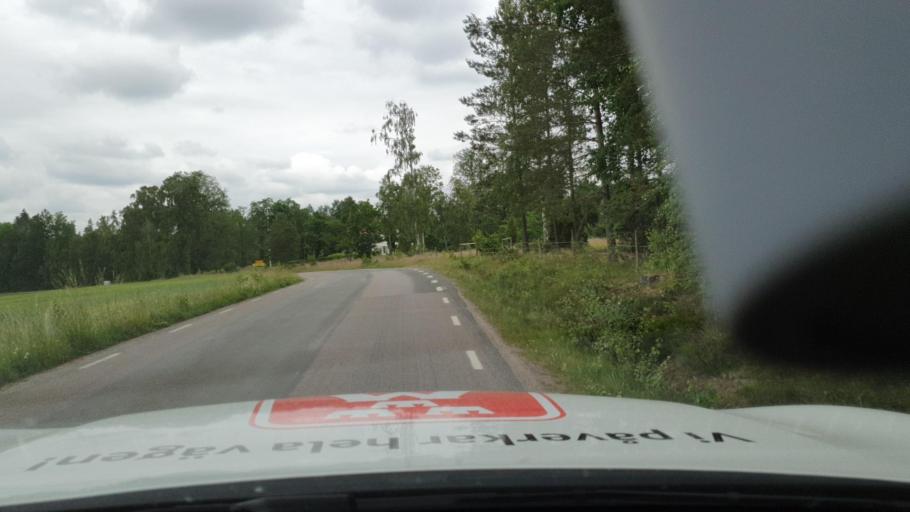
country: SE
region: Vaestra Goetaland
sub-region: Tidaholms Kommun
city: Olofstorp
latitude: 58.2467
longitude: 14.0984
